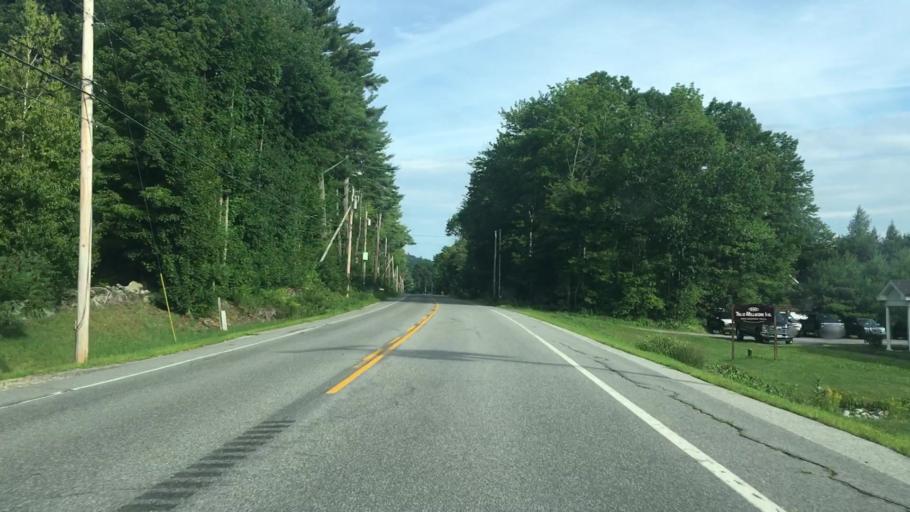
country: US
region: Maine
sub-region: York County
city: Limington
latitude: 43.7539
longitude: -70.6884
